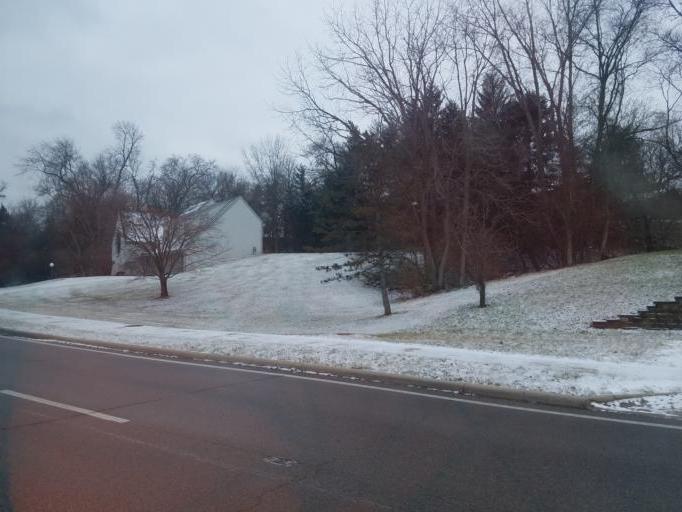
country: US
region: Ohio
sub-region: Franklin County
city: Worthington
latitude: 40.1203
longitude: -83.0352
